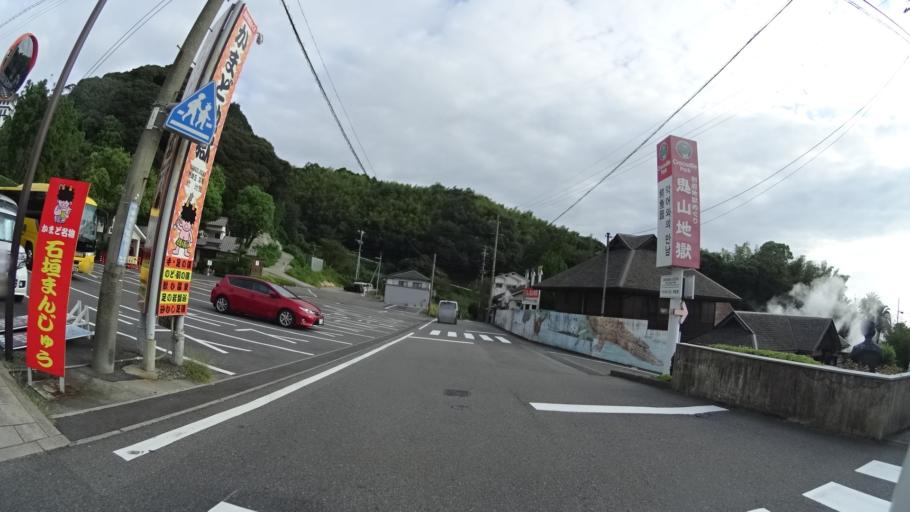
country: JP
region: Oita
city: Beppu
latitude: 33.3158
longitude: 131.4730
